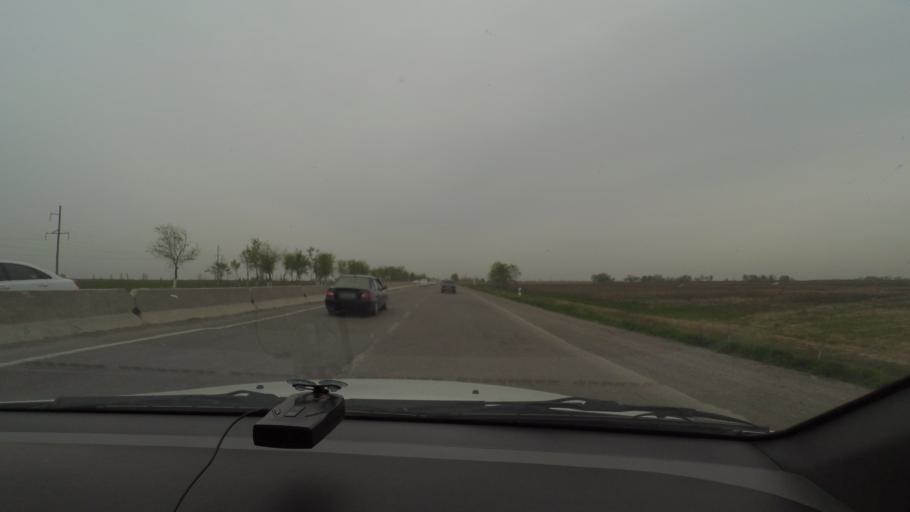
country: KZ
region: Ongtustik Qazaqstan
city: Myrzakent
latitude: 40.5299
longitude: 68.4401
